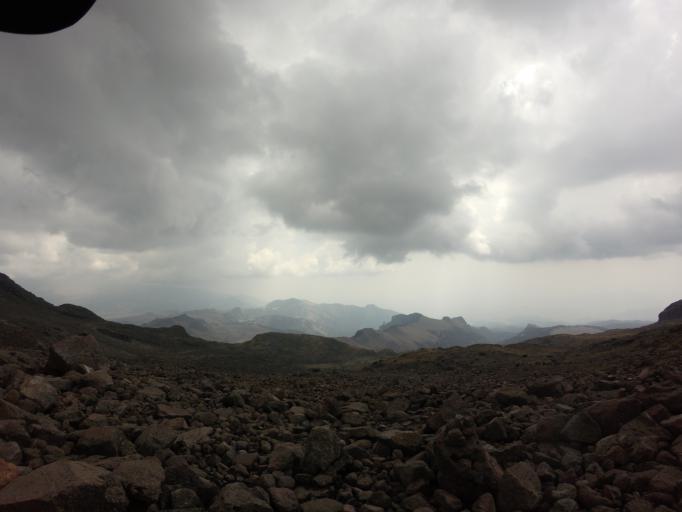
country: MX
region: Mexico
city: Amecameca de Juarez
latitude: 19.1575
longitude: -98.6434
